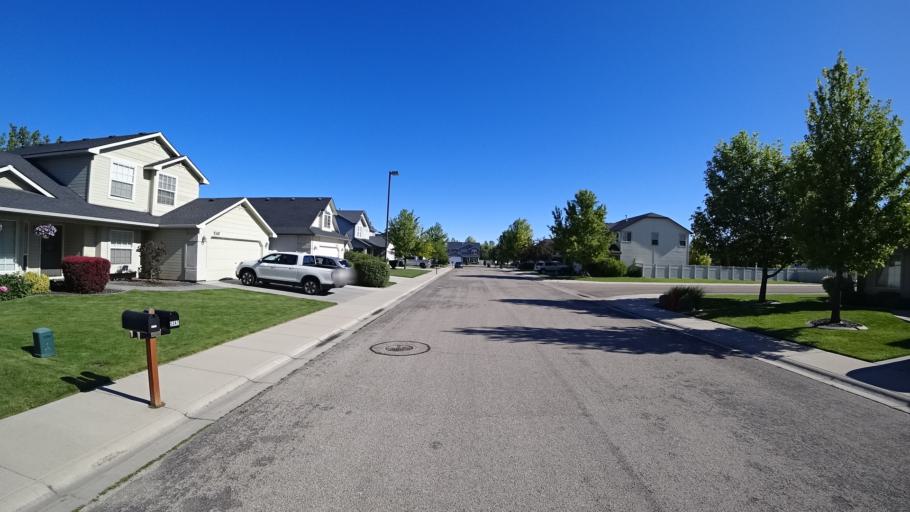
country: US
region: Idaho
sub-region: Ada County
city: Meridian
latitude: 43.6534
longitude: -116.4292
